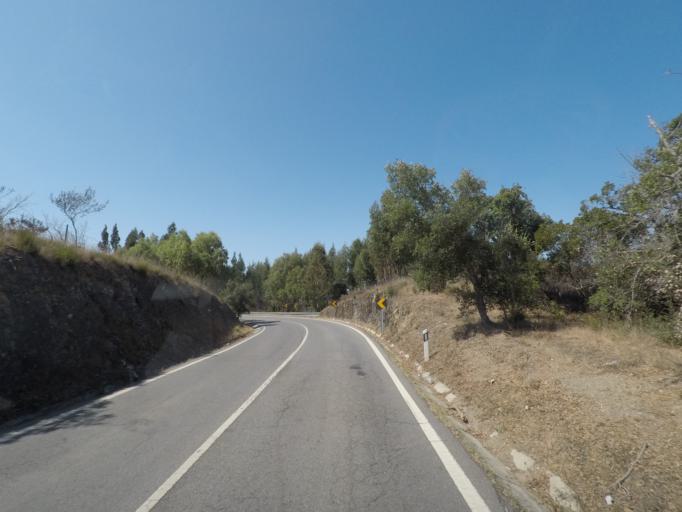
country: PT
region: Beja
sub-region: Odemira
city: Sao Teotonio
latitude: 37.5438
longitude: -8.6872
